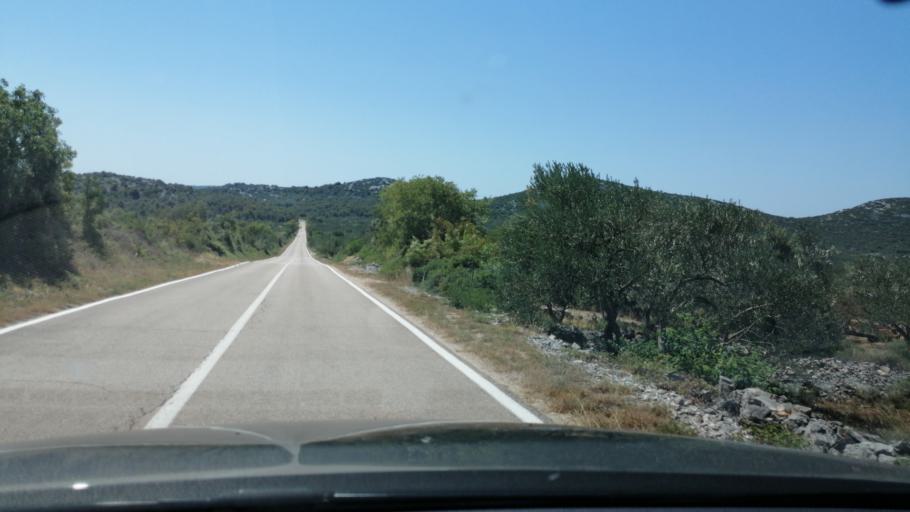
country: HR
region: Sibensko-Kniniska
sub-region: Grad Sibenik
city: Pirovac
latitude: 43.8527
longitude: 15.6880
